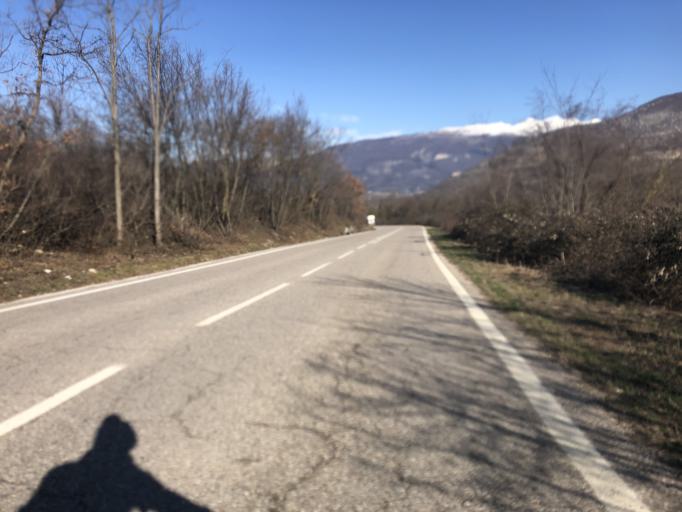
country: IT
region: Veneto
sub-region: Provincia di Verona
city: Volargne
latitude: 45.5441
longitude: 10.8371
